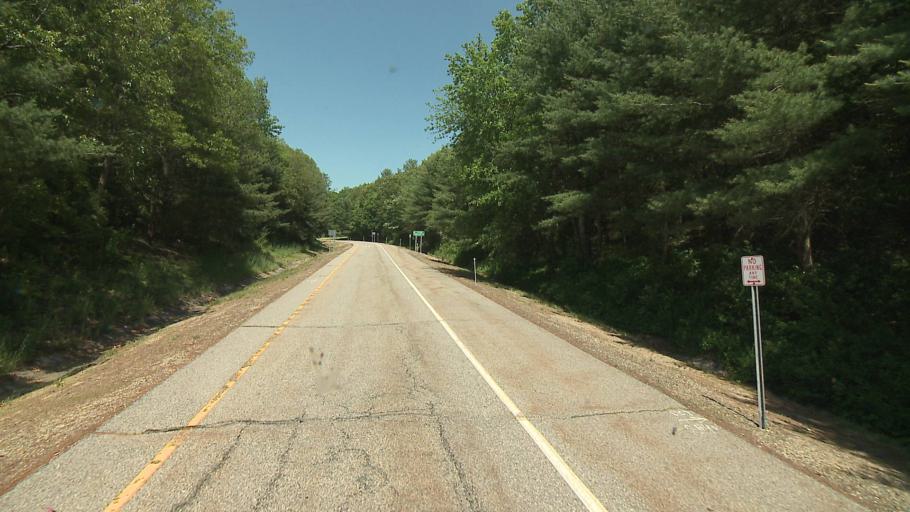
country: US
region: Connecticut
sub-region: Windham County
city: Putnam
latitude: 41.9079
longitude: -71.8915
